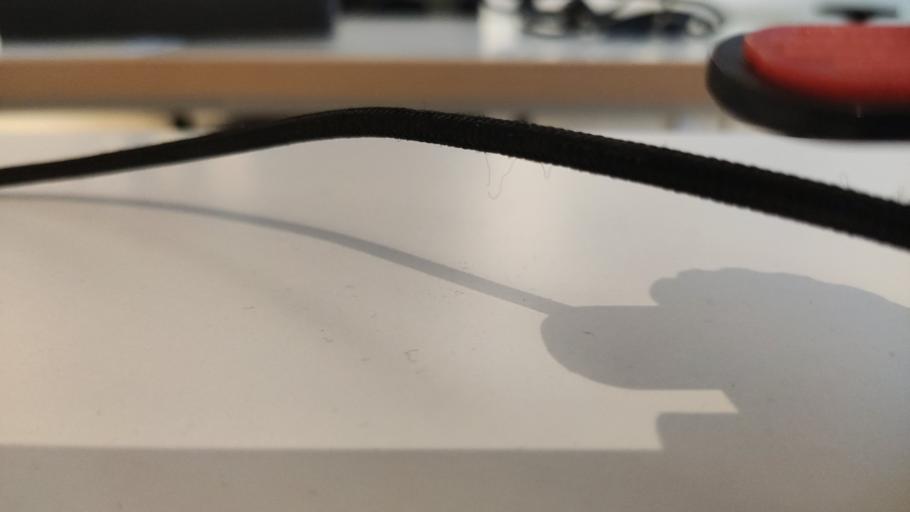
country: RU
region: Moskovskaya
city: Ruza
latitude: 55.7958
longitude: 36.2869
